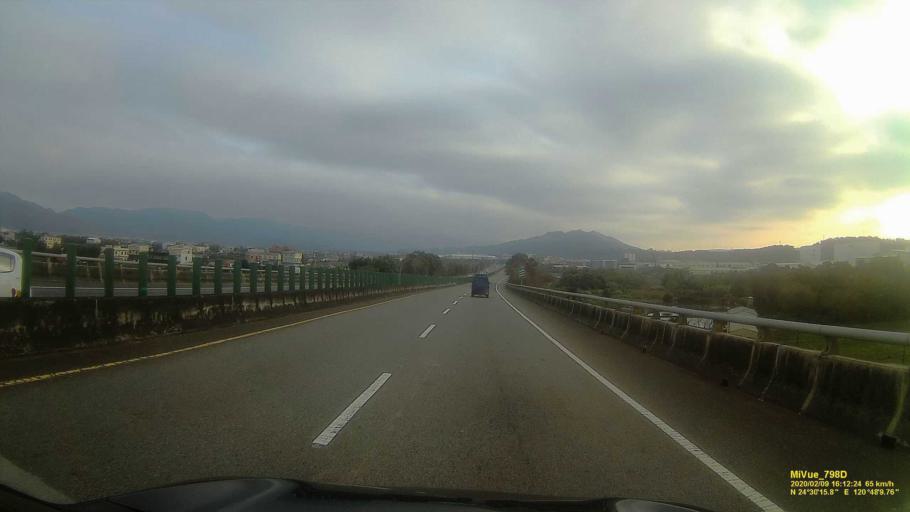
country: TW
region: Taiwan
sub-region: Miaoli
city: Miaoli
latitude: 24.5040
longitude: 120.8027
